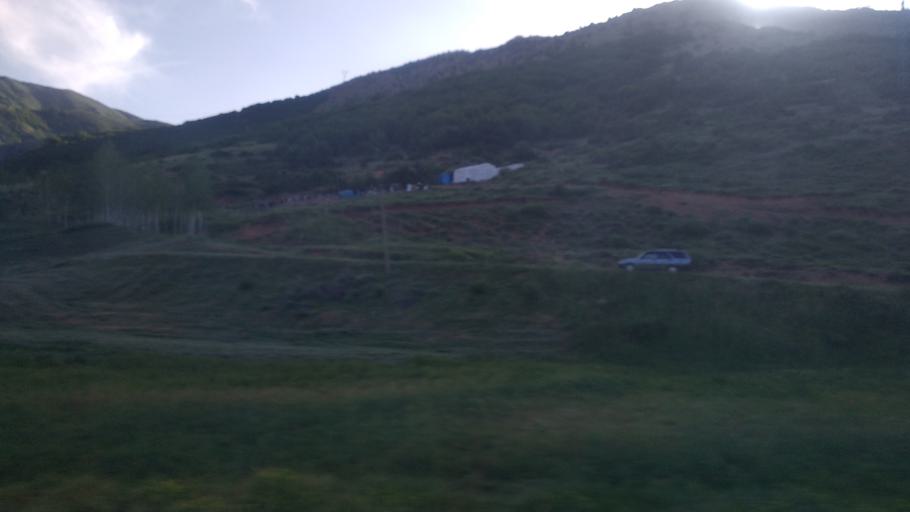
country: TR
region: Bitlis
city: Resadiye
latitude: 38.4537
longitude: 42.5418
